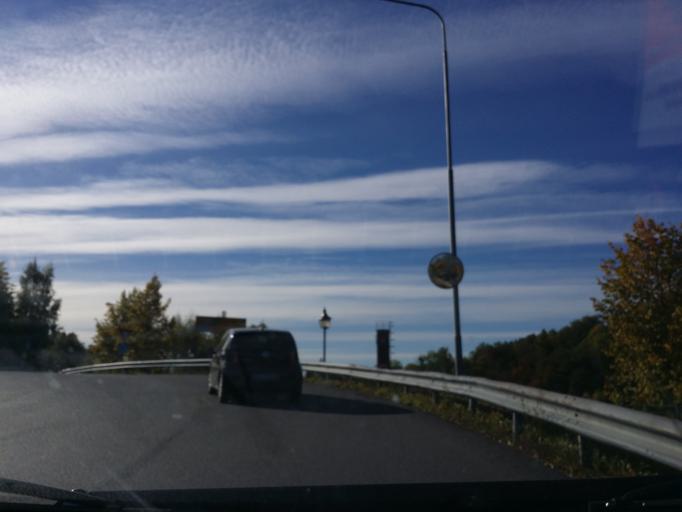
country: NO
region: Akershus
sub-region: Baerum
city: Skui
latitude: 59.9419
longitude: 10.5024
